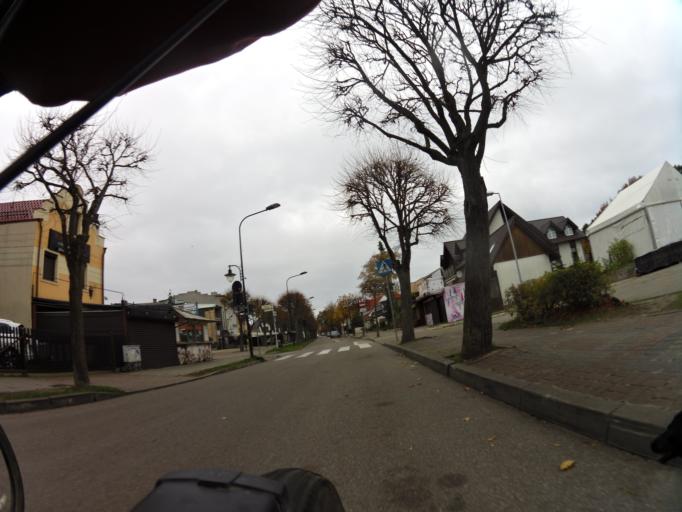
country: PL
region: Pomeranian Voivodeship
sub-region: Powiat pucki
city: Jastarnia
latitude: 54.6991
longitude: 18.6800
